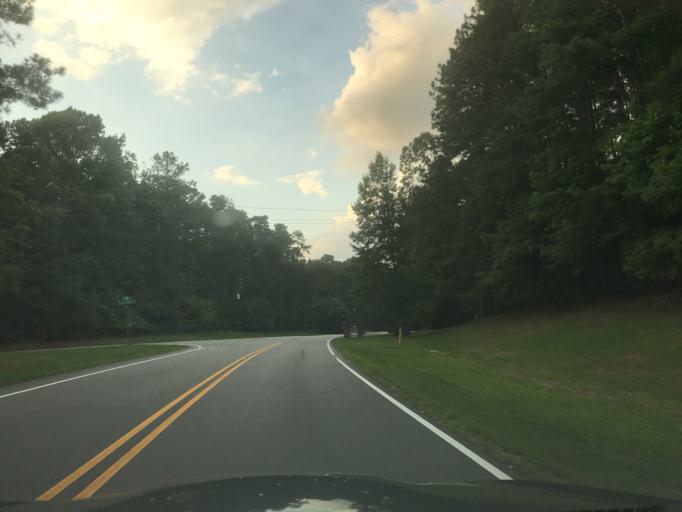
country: US
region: North Carolina
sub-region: Wake County
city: Wake Forest
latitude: 35.9386
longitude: -78.6105
